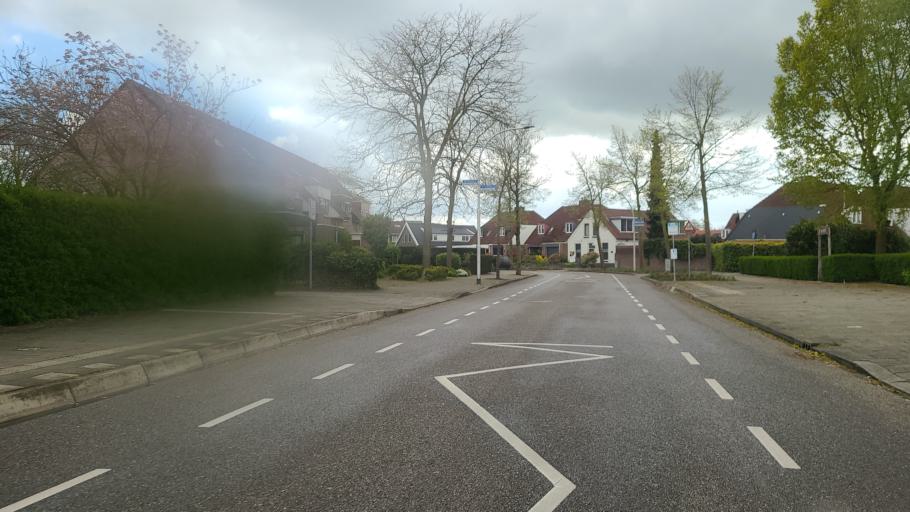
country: NL
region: Gelderland
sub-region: Gemeente Nijmegen
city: Lindenholt
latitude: 51.8336
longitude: 5.8029
